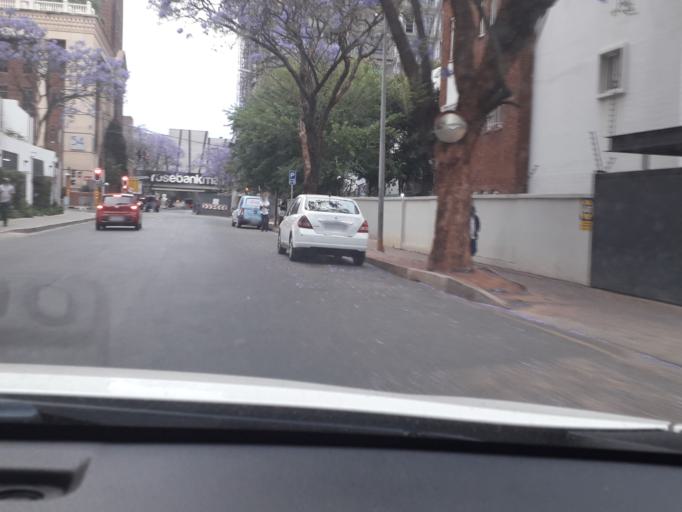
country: ZA
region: Gauteng
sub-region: City of Johannesburg Metropolitan Municipality
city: Johannesburg
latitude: -26.1447
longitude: 28.0402
